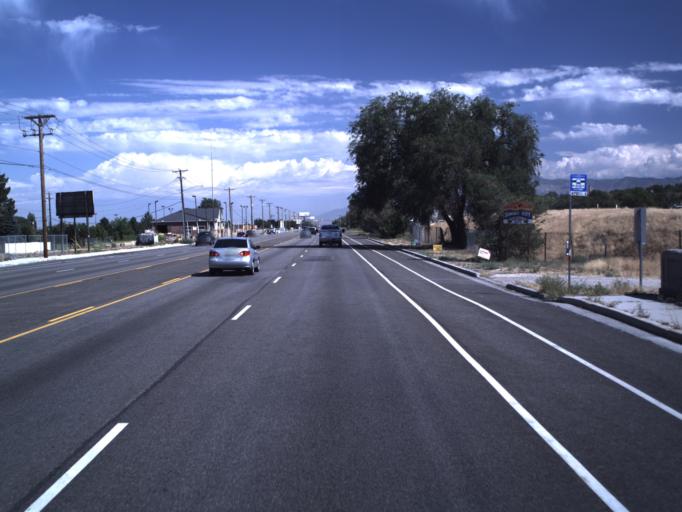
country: US
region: Utah
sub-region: Davis County
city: Sunset
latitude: 41.1257
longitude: -112.0259
